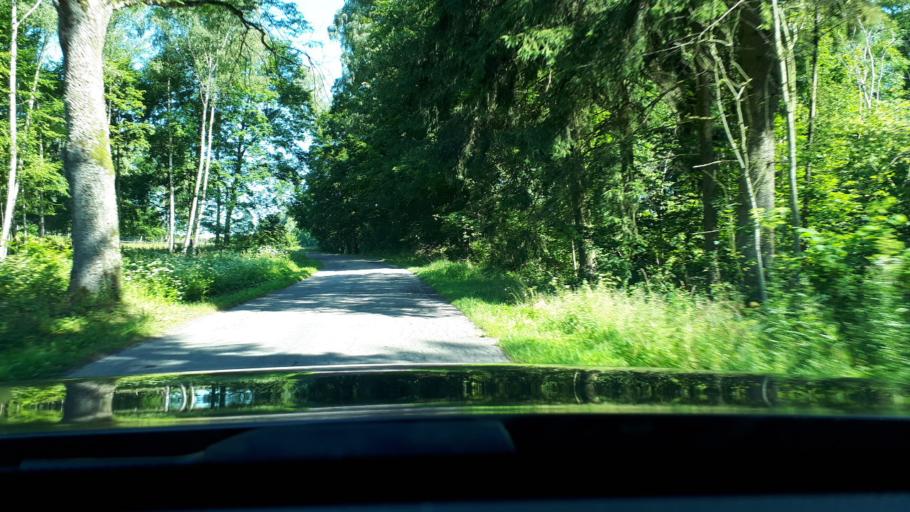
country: PL
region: Warmian-Masurian Voivodeship
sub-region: Powiat ostrodzki
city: Gierzwald
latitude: 53.6361
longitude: 20.1194
